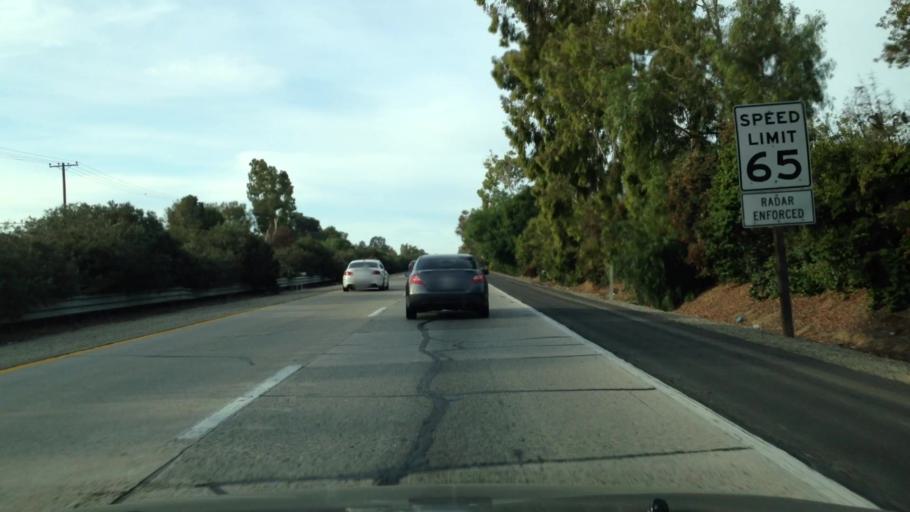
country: US
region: California
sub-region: Ventura County
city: Saticoy
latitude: 34.2846
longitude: -119.1650
